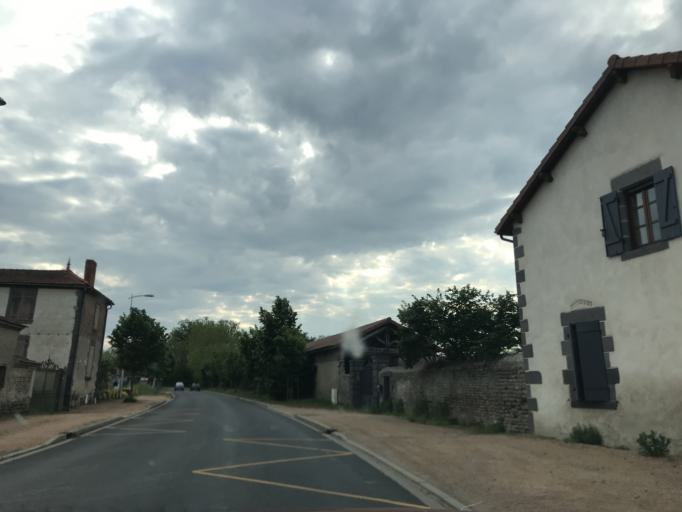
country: FR
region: Auvergne
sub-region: Departement du Puy-de-Dome
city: Maringues
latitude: 45.9210
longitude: 3.3436
